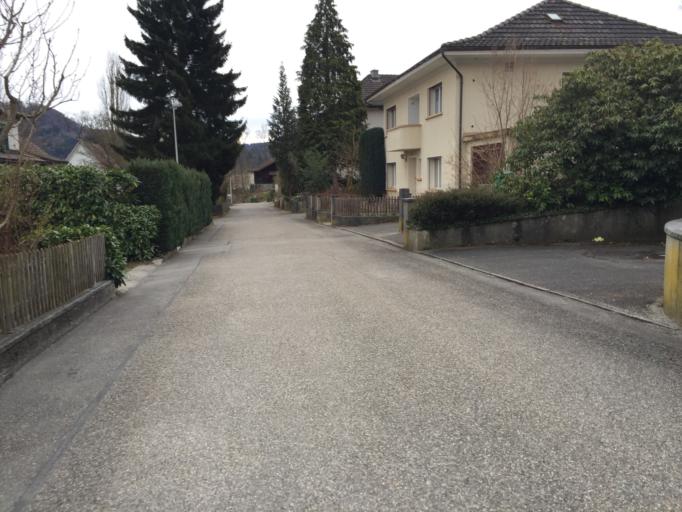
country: CH
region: Bern
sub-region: Bern-Mittelland District
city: Koniz
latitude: 46.9263
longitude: 7.4100
